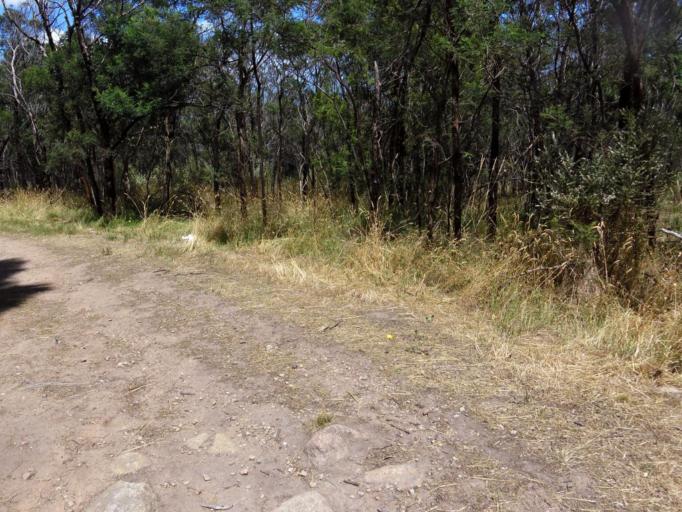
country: AU
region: Victoria
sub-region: Mornington Peninsula
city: Safety Beach
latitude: -38.2975
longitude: 144.9997
